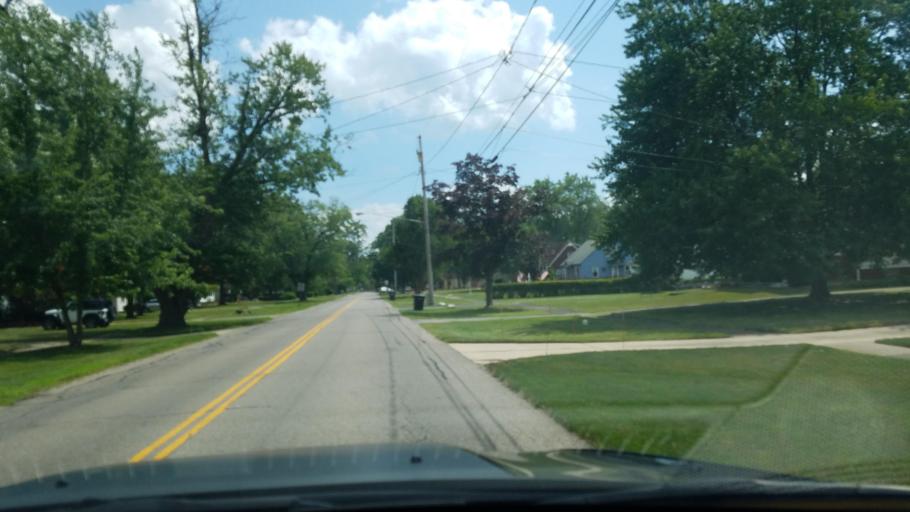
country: US
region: Ohio
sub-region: Trumbull County
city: Bolindale
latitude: 41.2297
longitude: -80.7849
